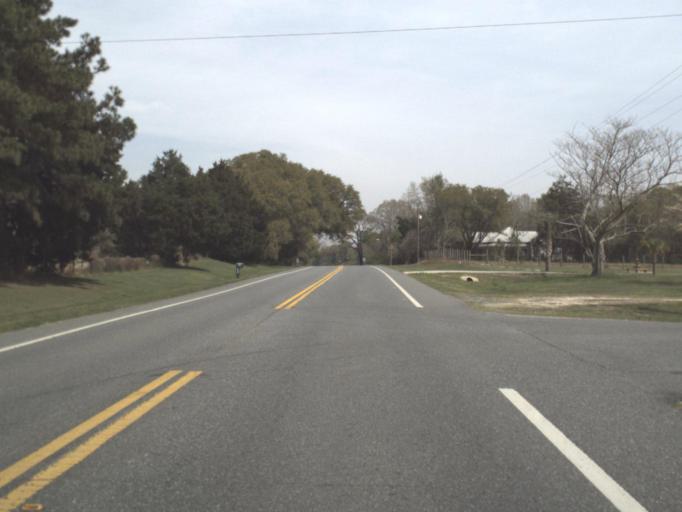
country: US
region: Florida
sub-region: Jackson County
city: Malone
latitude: 30.9571
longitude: -85.1543
